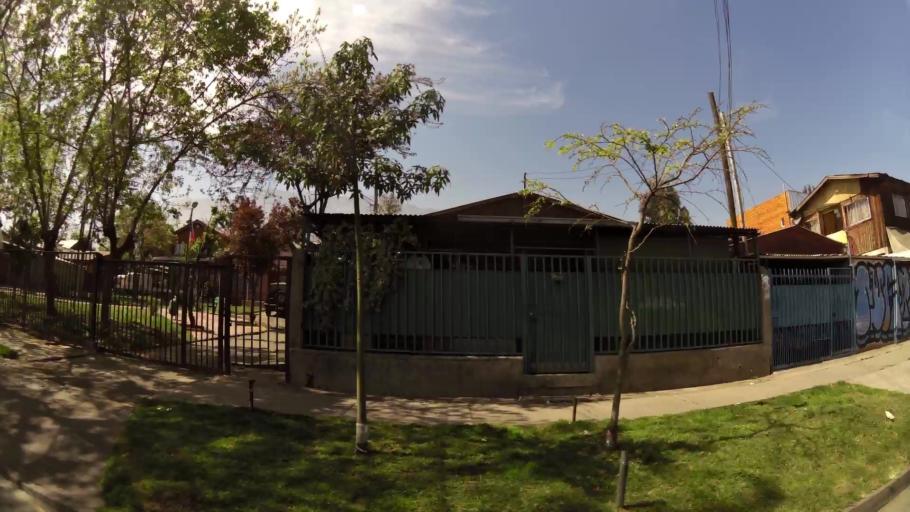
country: CL
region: Santiago Metropolitan
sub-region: Provincia de Santiago
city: Villa Presidente Frei, Nunoa, Santiago, Chile
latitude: -33.4723
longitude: -70.5361
